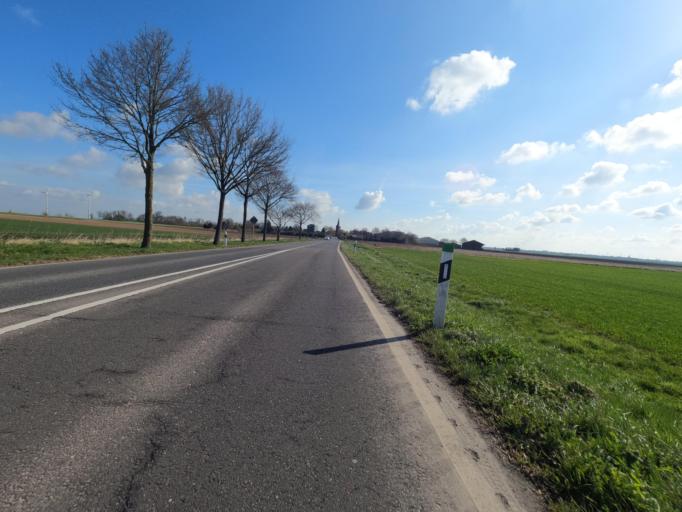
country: DE
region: North Rhine-Westphalia
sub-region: Regierungsbezirk Koln
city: Linnich
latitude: 50.9958
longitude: 6.3383
